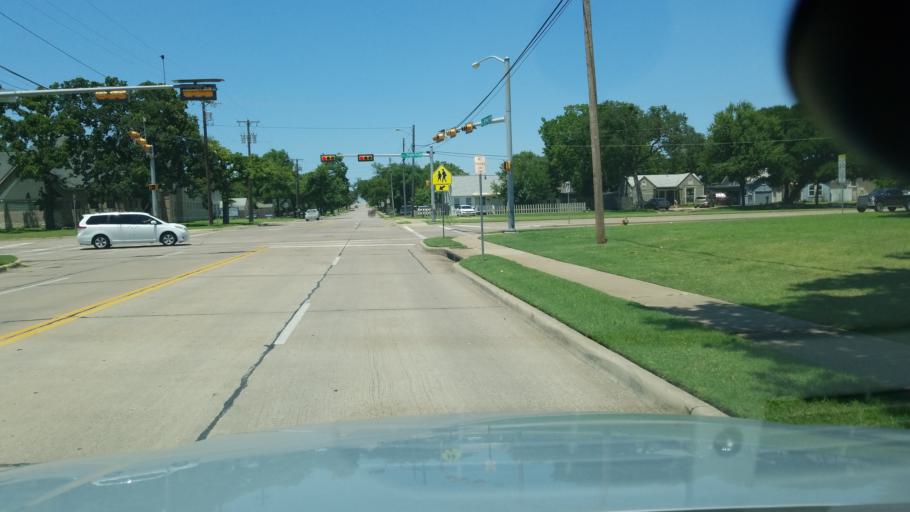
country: US
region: Texas
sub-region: Dallas County
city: Irving
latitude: 32.8006
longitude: -96.9257
